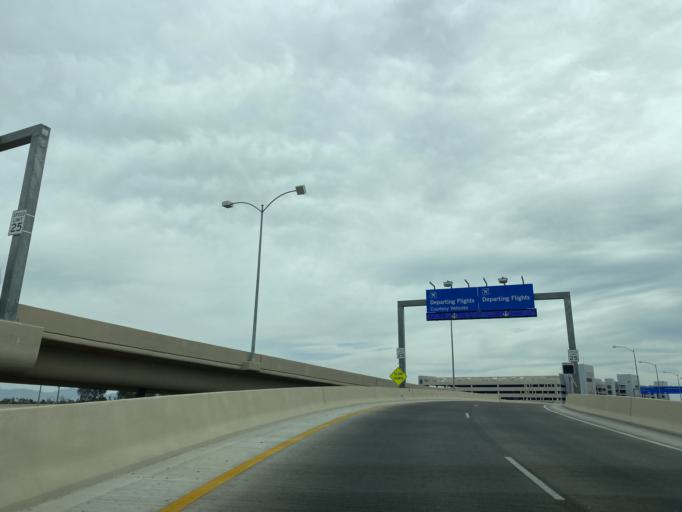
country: US
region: Nevada
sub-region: Clark County
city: Paradise
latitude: 36.0865
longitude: -115.1424
